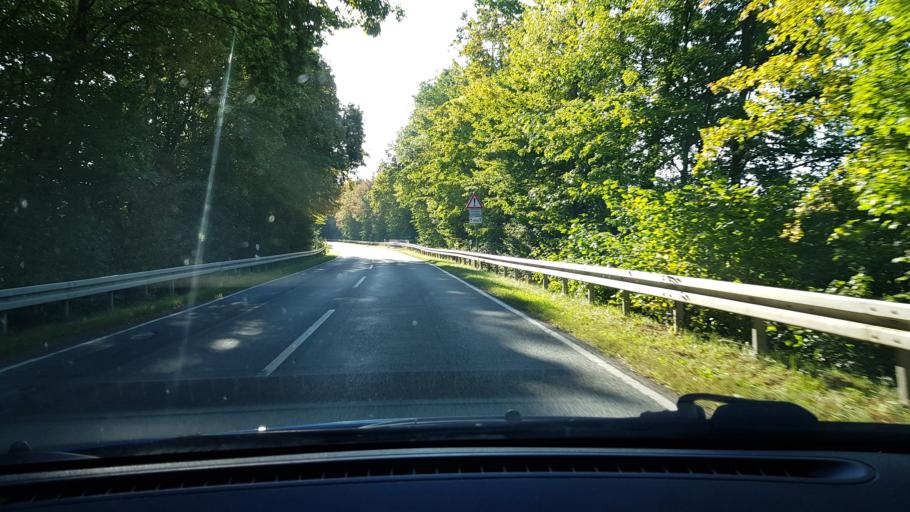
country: DE
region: Lower Saxony
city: Pohle
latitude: 52.2590
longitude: 9.3529
